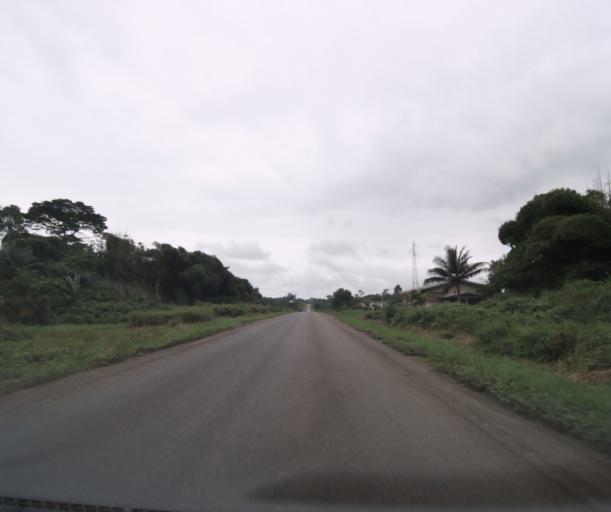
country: CM
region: Littoral
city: Edea
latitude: 3.7348
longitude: 10.1151
